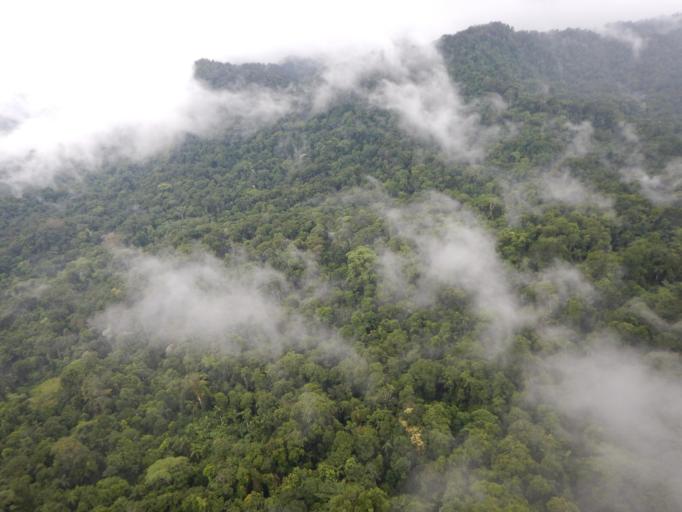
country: BO
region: Santa Cruz
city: Comarapa
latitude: -17.4178
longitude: -64.3752
